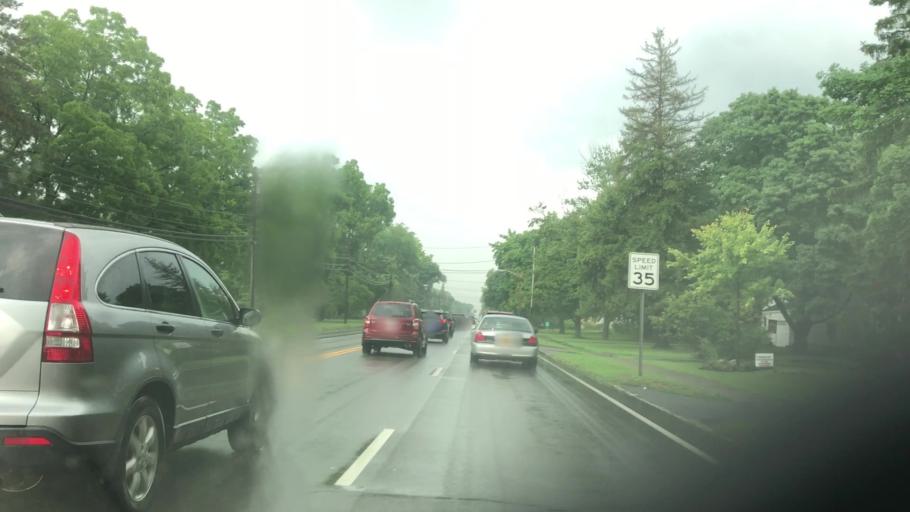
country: US
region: New York
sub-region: Monroe County
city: East Rochester
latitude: 43.1313
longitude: -77.4680
